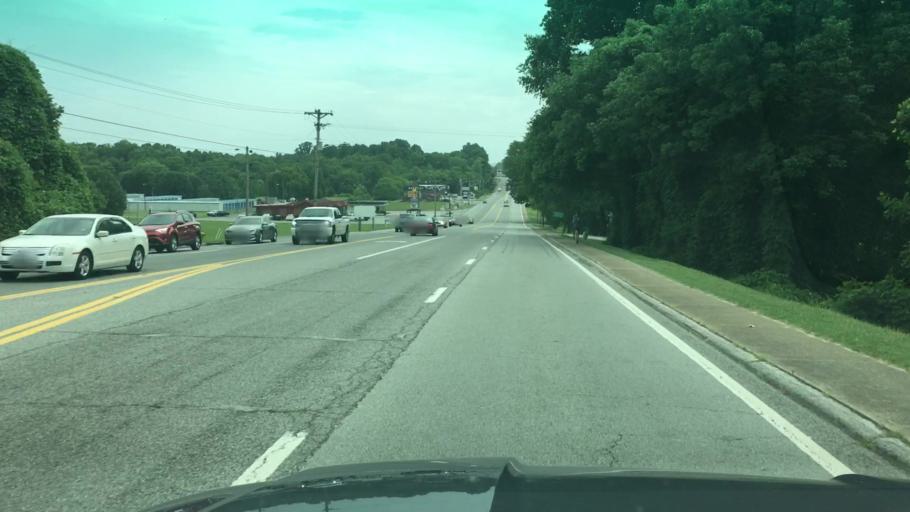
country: US
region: Tennessee
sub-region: Coffee County
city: Manchester
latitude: 35.4852
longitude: -86.0768
